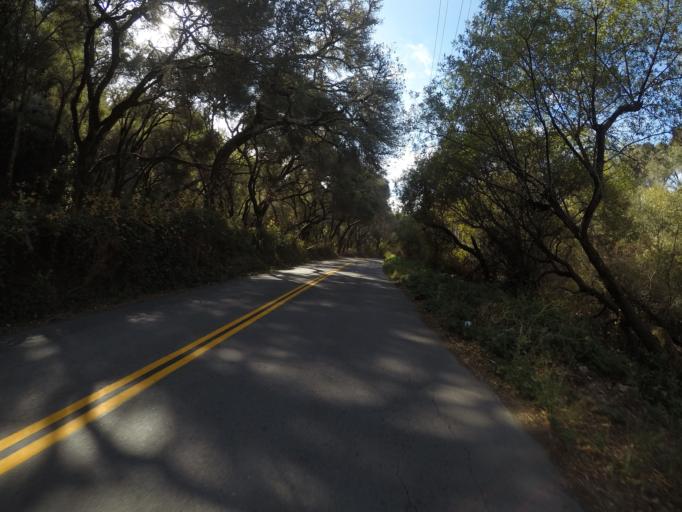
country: US
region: California
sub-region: Santa Cruz County
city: Soquel
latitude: 37.0088
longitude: -121.9658
